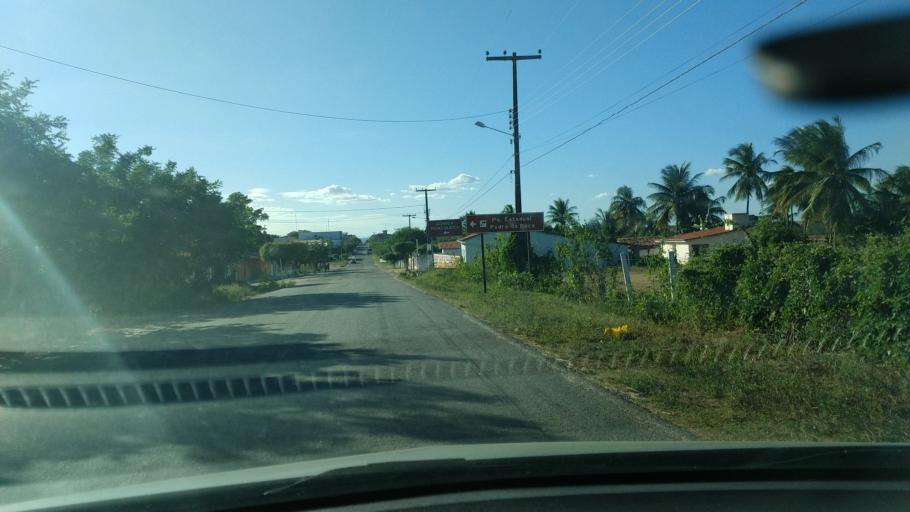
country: BR
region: Rio Grande do Norte
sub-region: Sao Jose Do Campestre
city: Sao Jose do Campestre
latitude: -6.4416
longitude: -35.6416
